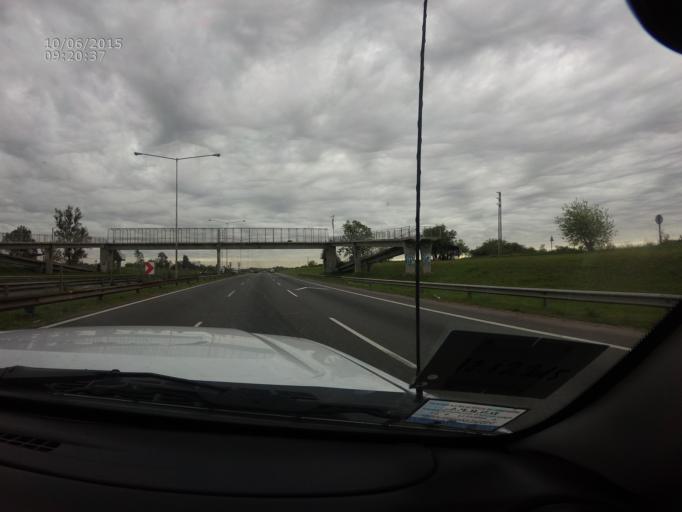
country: AR
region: Buenos Aires
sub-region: Partido de Campana
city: Campana
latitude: -34.2478
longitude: -58.9079
